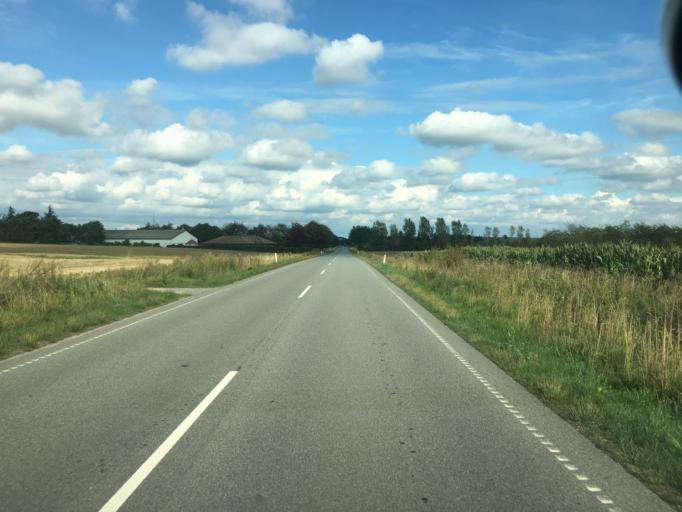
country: DK
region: South Denmark
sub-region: Tonder Kommune
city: Logumkloster
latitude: 55.0476
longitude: 8.9280
